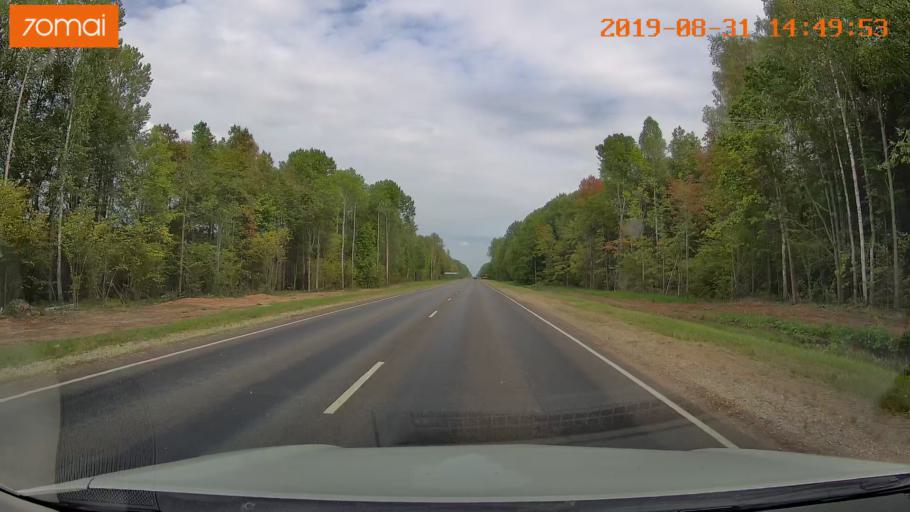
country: RU
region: Kaluga
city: Spas-Demensk
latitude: 54.2574
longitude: 33.7761
